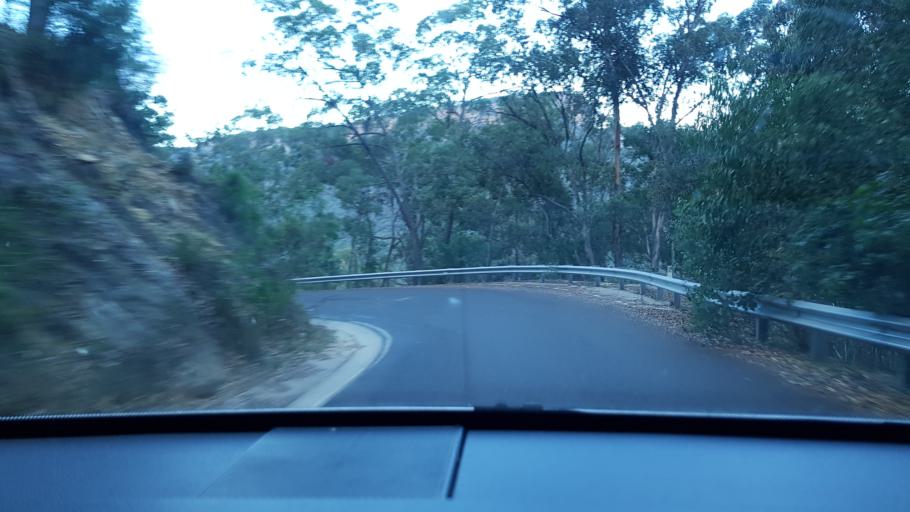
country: AU
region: New South Wales
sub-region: Lithgow
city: Portland
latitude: -33.3088
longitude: 150.1136
